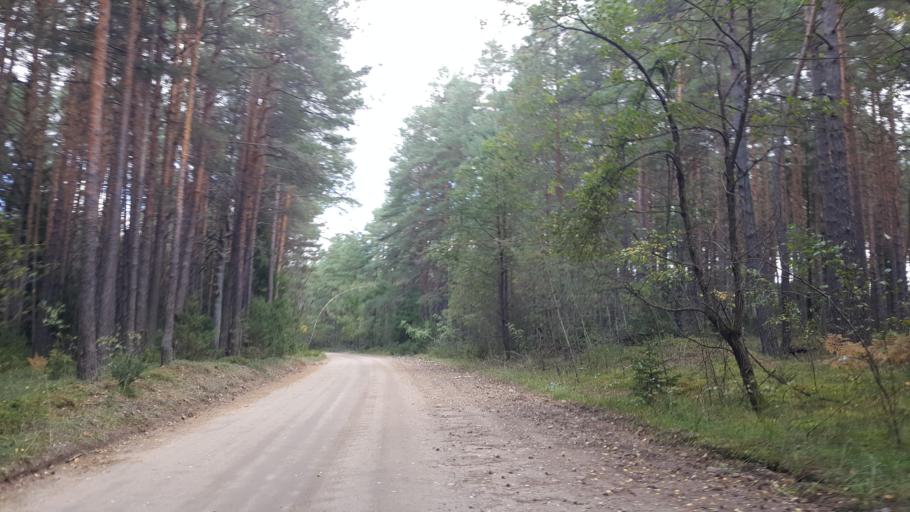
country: BY
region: Brest
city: Kamyanyets
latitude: 52.4245
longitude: 23.9420
